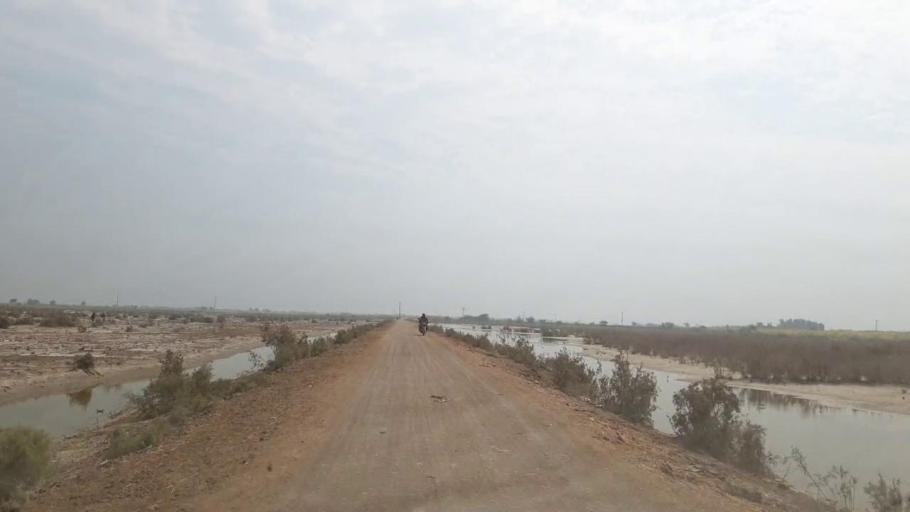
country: PK
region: Sindh
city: Mirpur Khas
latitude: 25.5549
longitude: 69.1217
